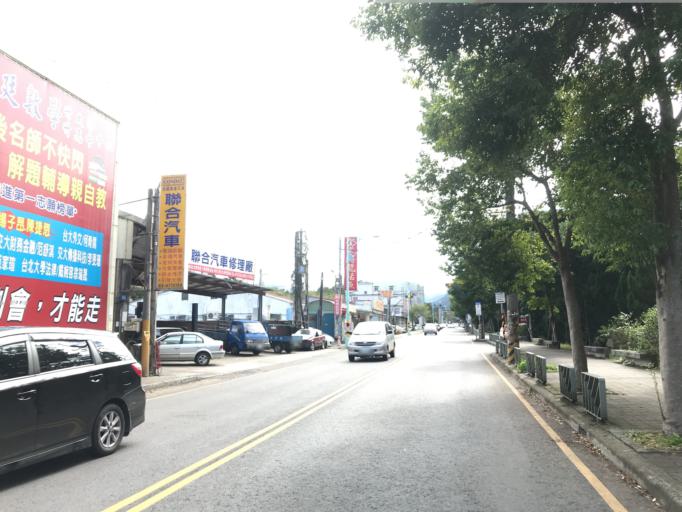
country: TW
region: Taiwan
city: Daxi
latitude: 24.8416
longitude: 121.2406
